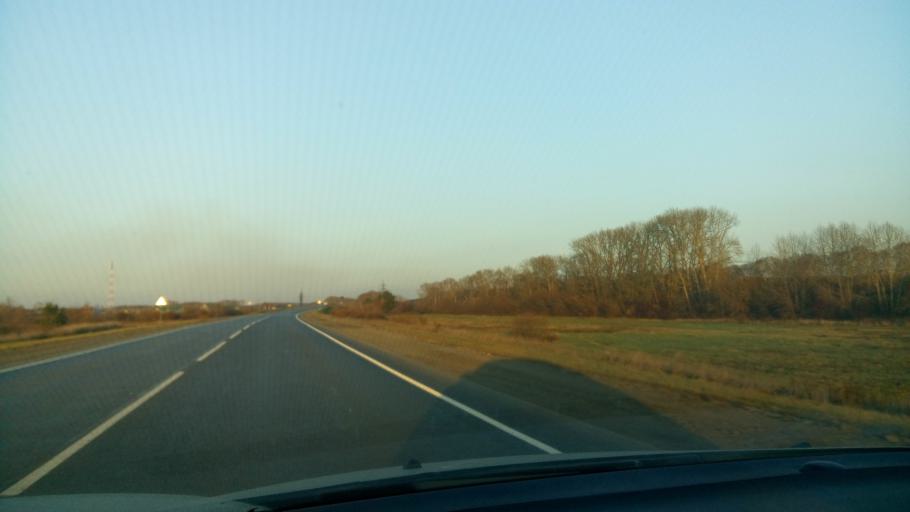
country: RU
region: Sverdlovsk
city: Obukhovskoye
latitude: 56.8366
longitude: 62.5757
